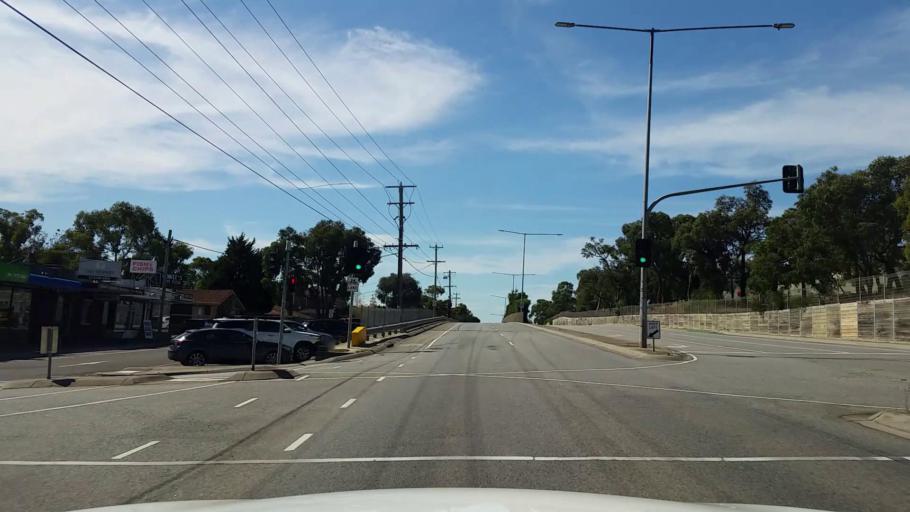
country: AU
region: Victoria
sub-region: Frankston
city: Langwarrin
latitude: -38.1464
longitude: 145.2010
